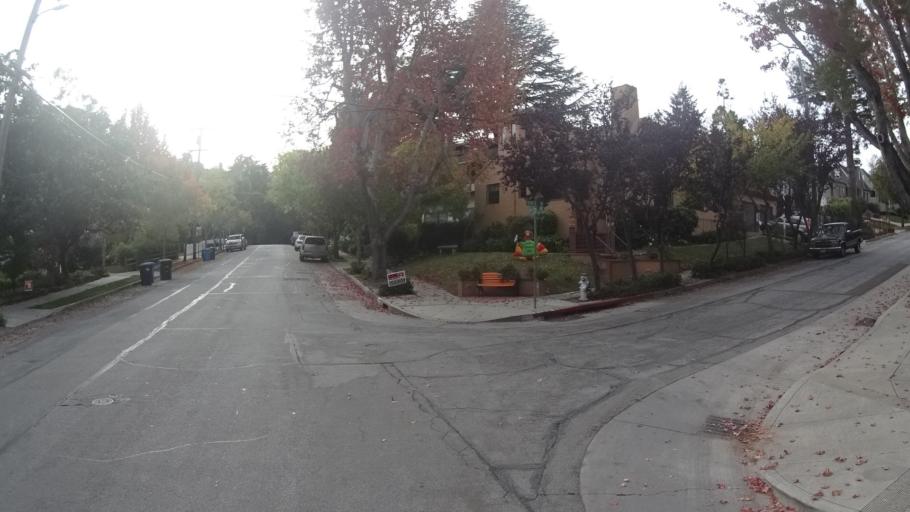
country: US
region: California
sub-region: San Mateo County
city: Hillsborough
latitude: 37.5785
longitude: -122.3776
